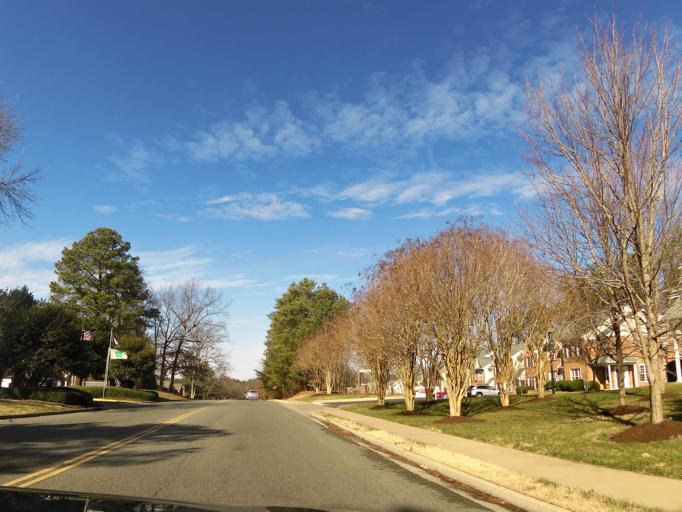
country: US
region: Virginia
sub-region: Henrico County
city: Tuckahoe
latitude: 37.6278
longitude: -77.5525
